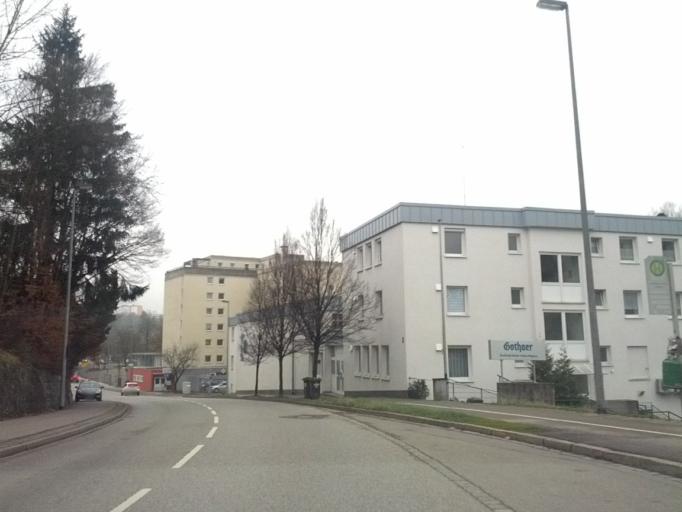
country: DE
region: Bavaria
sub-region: Swabia
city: Kempten (Allgaeu)
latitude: 47.7274
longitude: 10.3220
